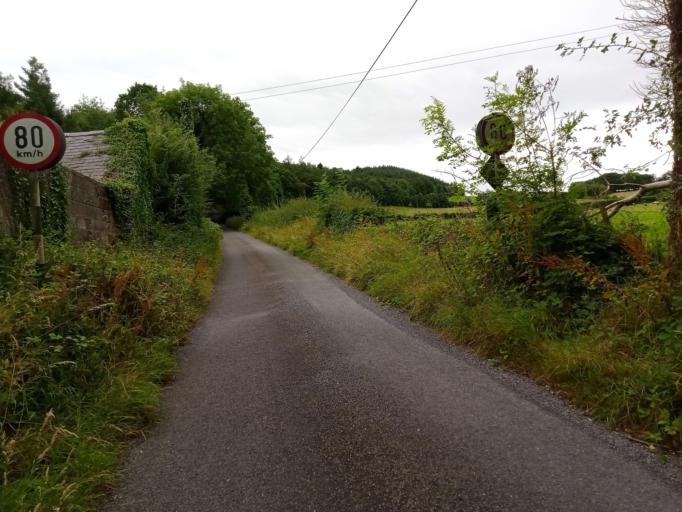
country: IE
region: Leinster
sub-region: Laois
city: Abbeyleix
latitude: 52.8324
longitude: -7.3936
